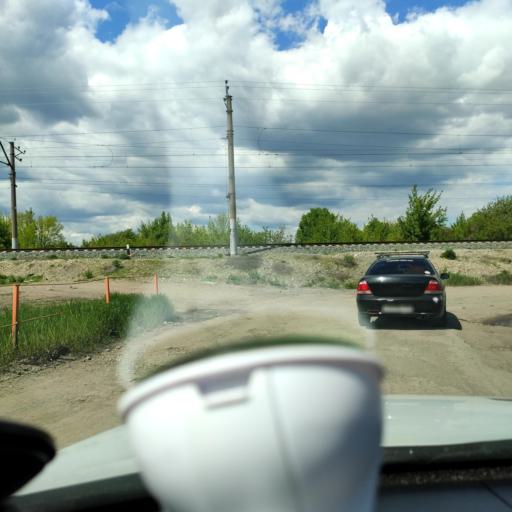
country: RU
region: Samara
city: Petra-Dubrava
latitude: 53.2659
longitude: 50.3153
